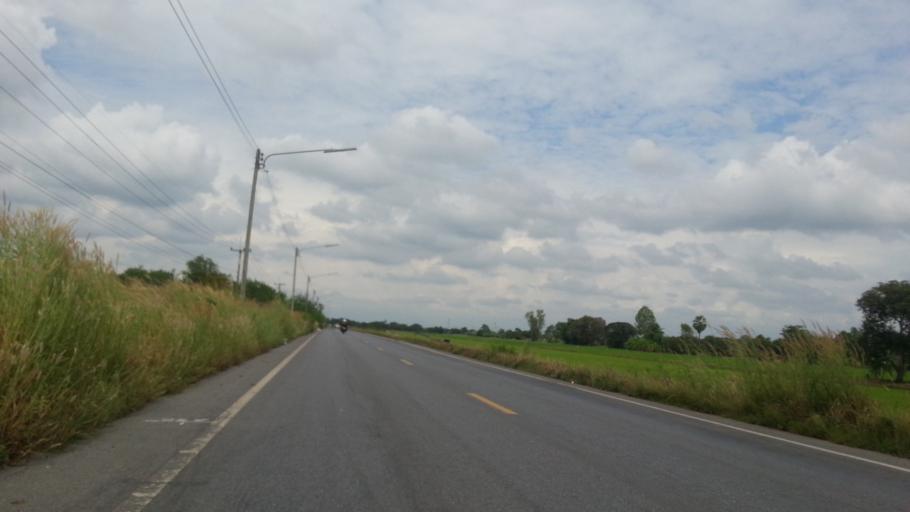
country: TH
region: Pathum Thani
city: Ban Rangsit
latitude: 14.0440
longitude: 100.8445
